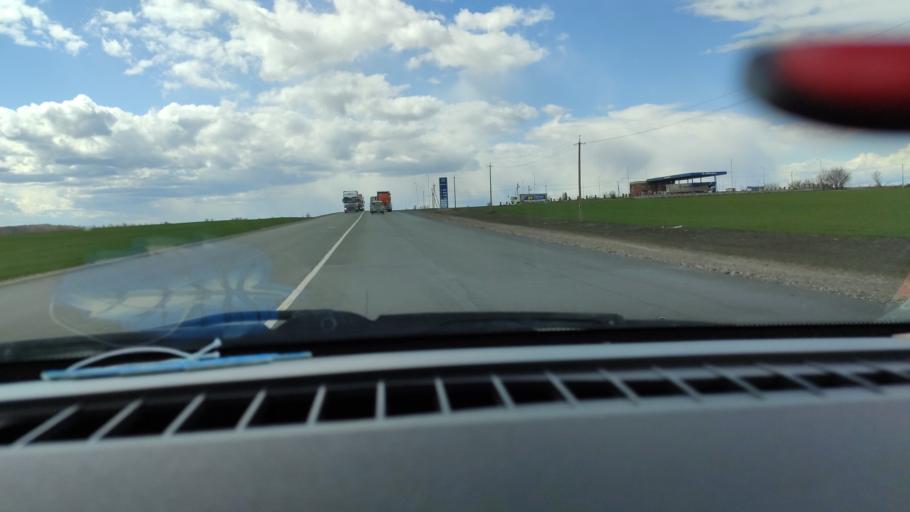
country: RU
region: Samara
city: Varlamovo
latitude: 53.2115
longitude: 48.4507
